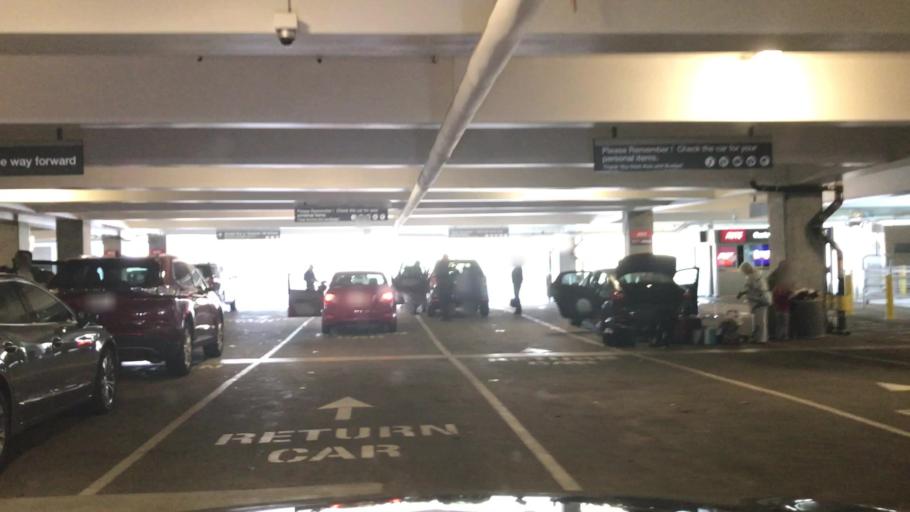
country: US
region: Washington
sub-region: King County
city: SeaTac
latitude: 47.4621
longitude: -122.2924
